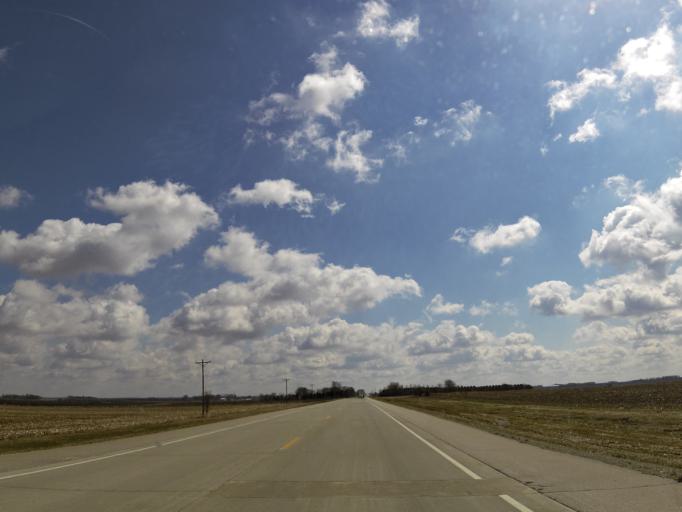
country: US
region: Minnesota
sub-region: Dodge County
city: Dodge Center
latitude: 44.1335
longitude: -92.8996
